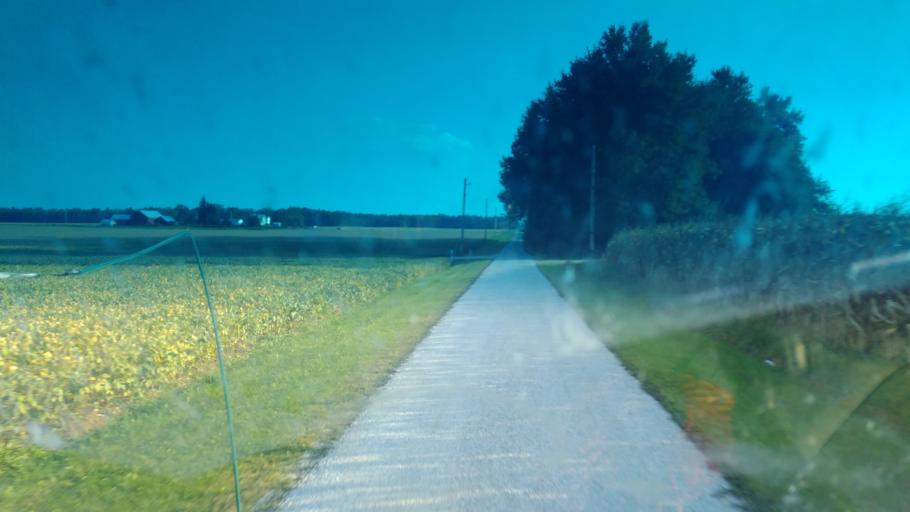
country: US
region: Ohio
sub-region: Crawford County
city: Bucyrus
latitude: 40.9400
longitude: -82.9973
